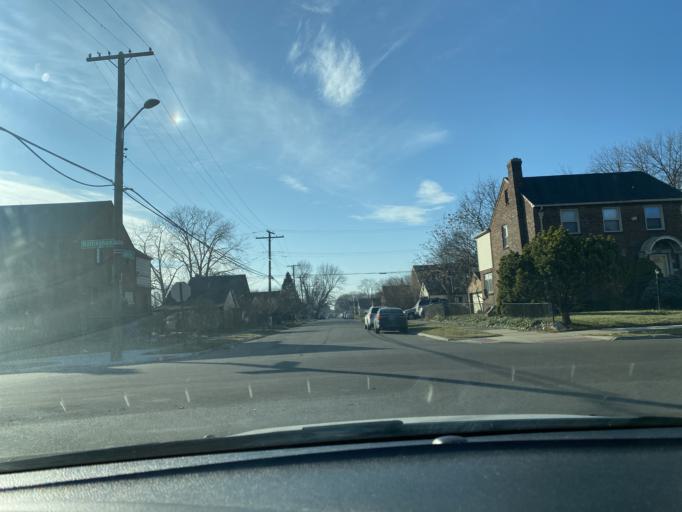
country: US
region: Michigan
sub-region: Wayne County
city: Grosse Pointe Park
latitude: 42.4057
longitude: -82.9531
